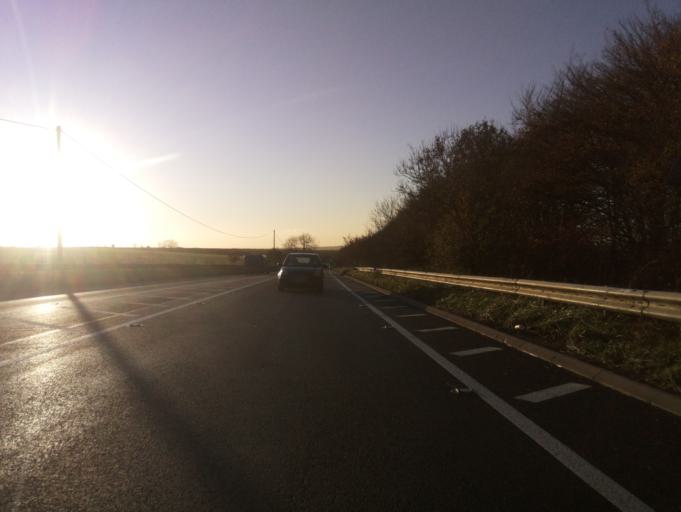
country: GB
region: England
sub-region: Wiltshire
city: Chicklade
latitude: 51.1011
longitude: -2.1895
